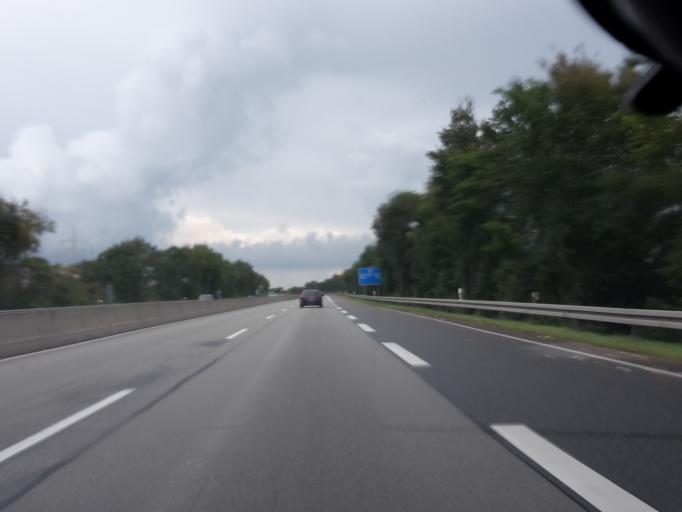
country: DE
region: Rheinland-Pfalz
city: Mainz
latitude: 50.0295
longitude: 8.2995
